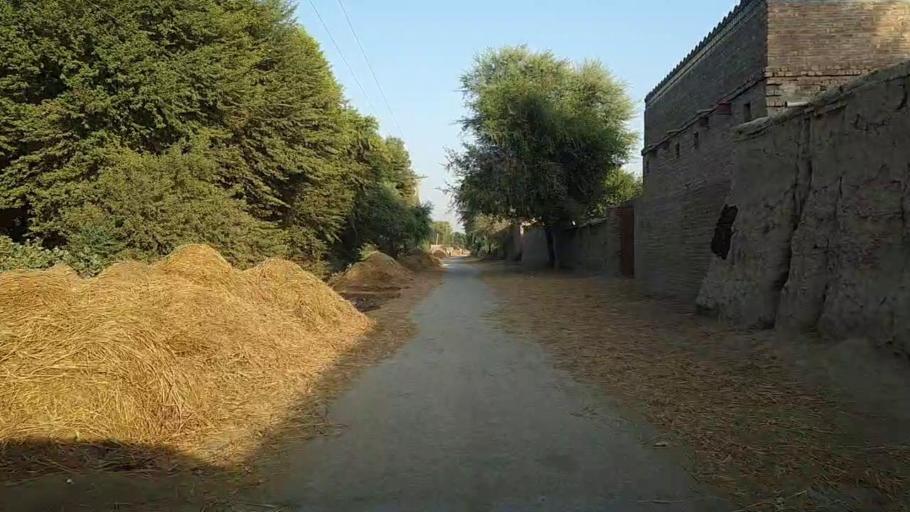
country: PK
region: Sindh
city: Kashmor
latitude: 28.4284
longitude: 69.4643
